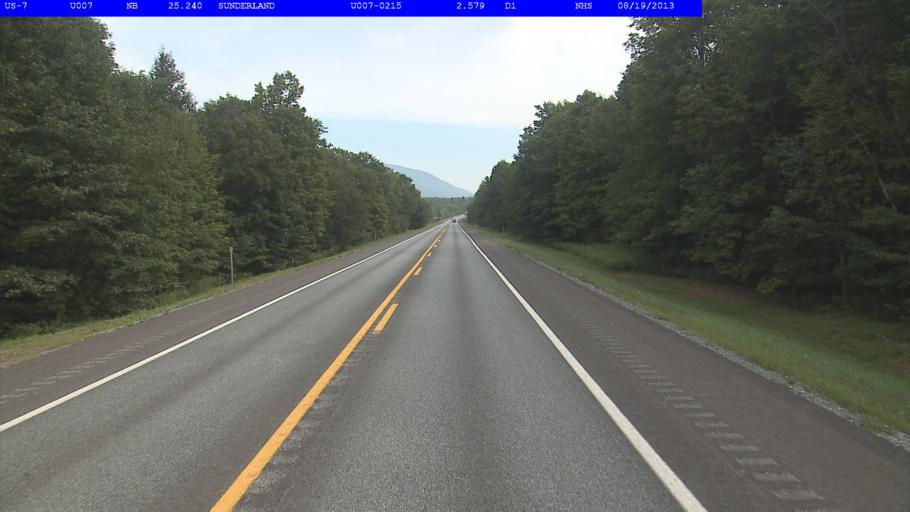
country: US
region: Vermont
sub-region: Bennington County
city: Arlington
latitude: 43.0614
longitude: -73.1249
